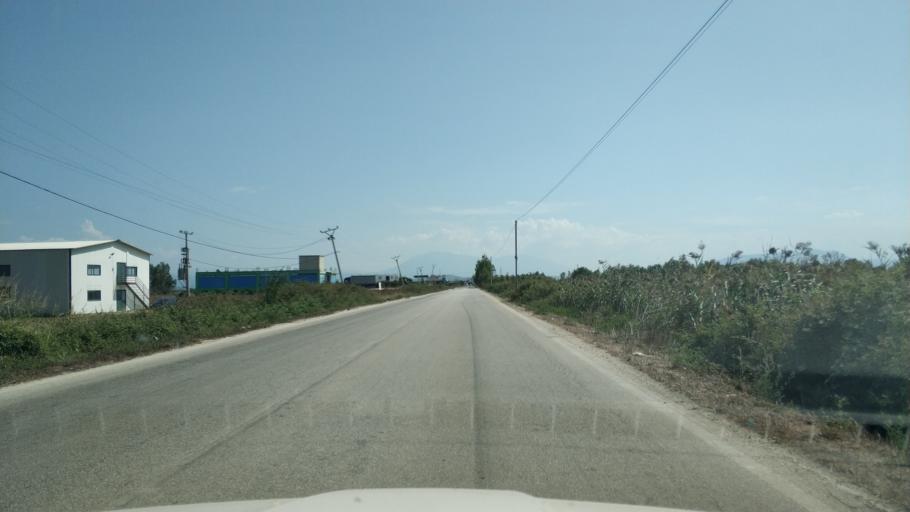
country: AL
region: Fier
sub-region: Rrethi i Lushnjes
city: Krutja e Poshtme
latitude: 40.8831
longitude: 19.6588
